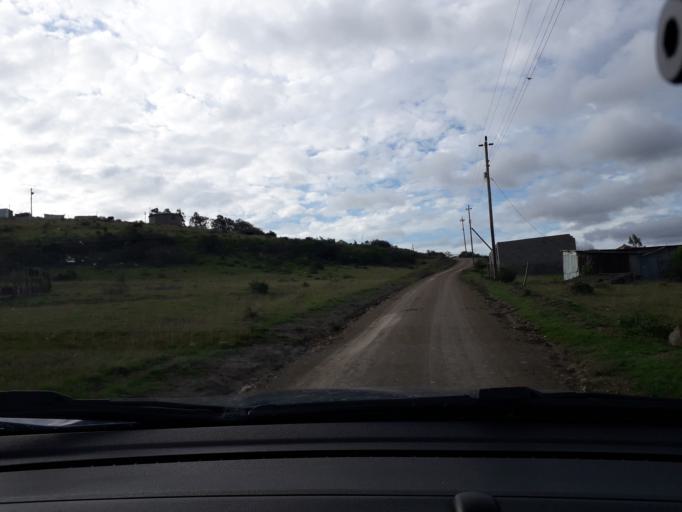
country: ZA
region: Eastern Cape
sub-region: Buffalo City Metropolitan Municipality
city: East London
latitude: -32.8021
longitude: 27.9618
